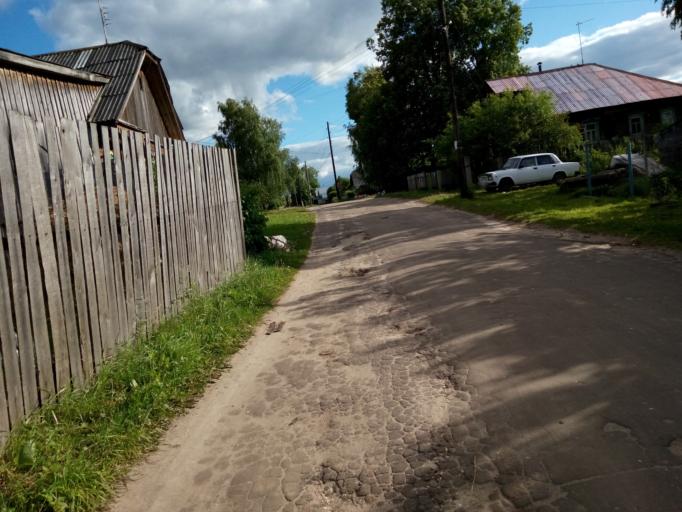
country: RU
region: Nizjnij Novgorod
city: Voskresenskoye
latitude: 56.7848
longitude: 45.5140
